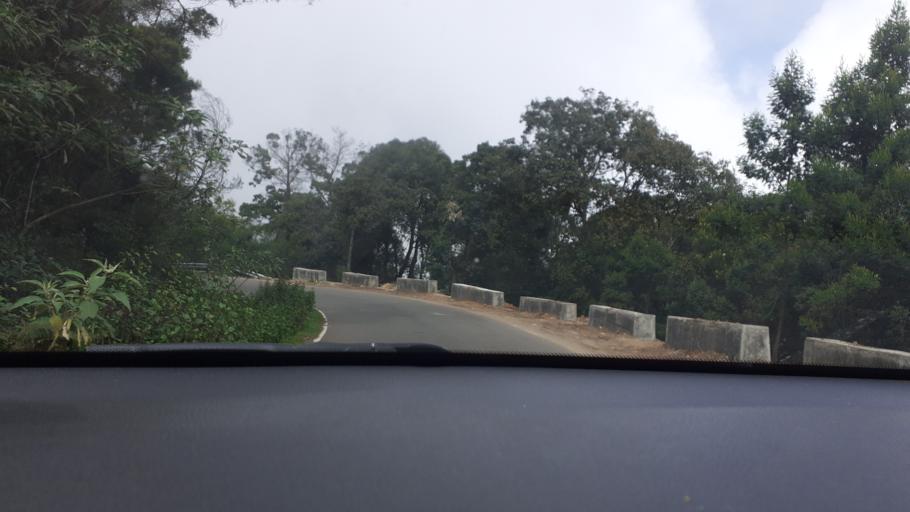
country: IN
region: Tamil Nadu
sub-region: Dindigul
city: Kodaikanal
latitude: 10.2447
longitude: 77.4203
